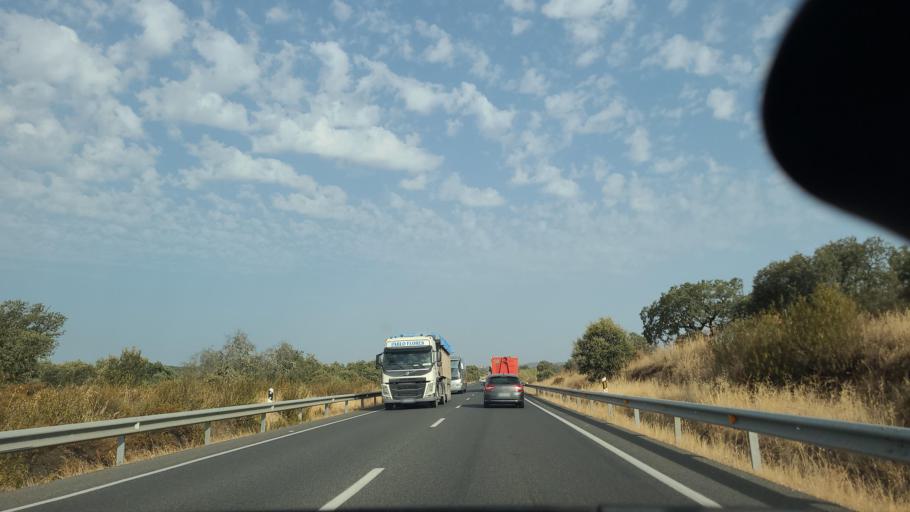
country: ES
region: Andalusia
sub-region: Province of Cordoba
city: Obejo
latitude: 38.0573
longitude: -4.8163
